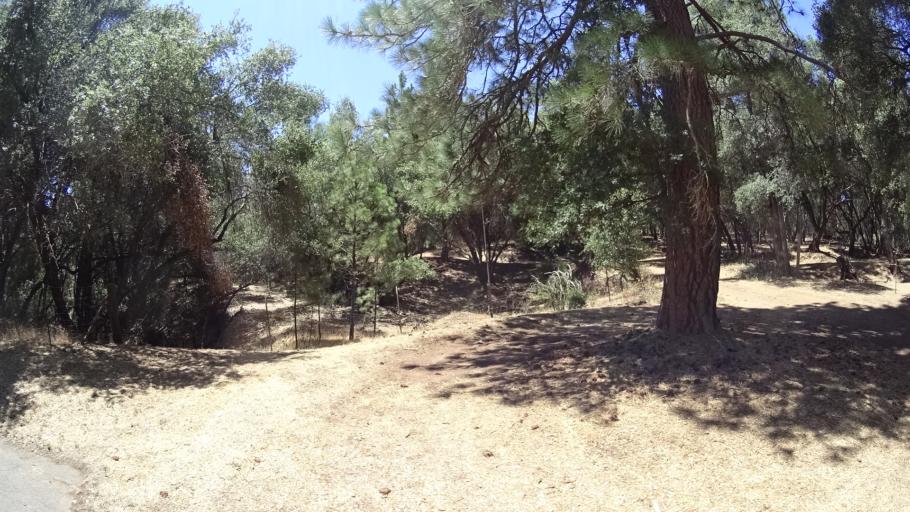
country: US
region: California
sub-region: Calaveras County
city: Mountain Ranch
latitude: 38.2257
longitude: -120.5406
